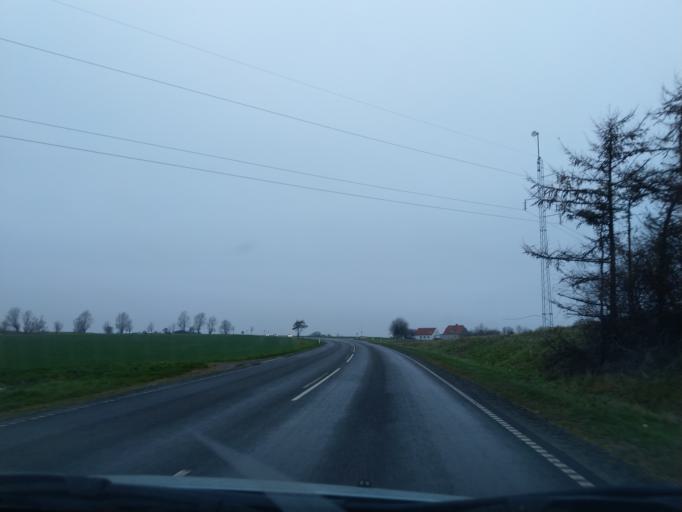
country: DK
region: Zealand
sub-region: Vordingborg Kommune
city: Praesto
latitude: 55.1177
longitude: 12.0252
